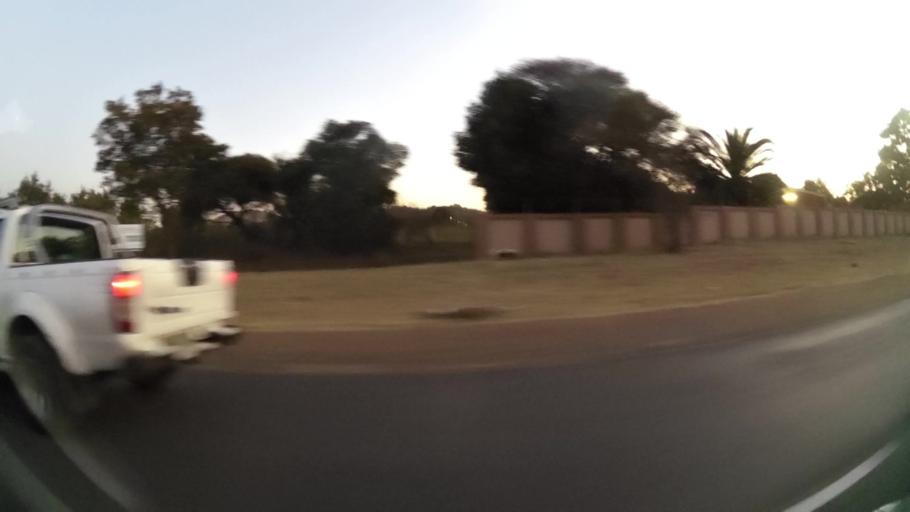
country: ZA
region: North-West
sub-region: Bojanala Platinum District Municipality
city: Rustenburg
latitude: -25.6772
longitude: 27.2503
